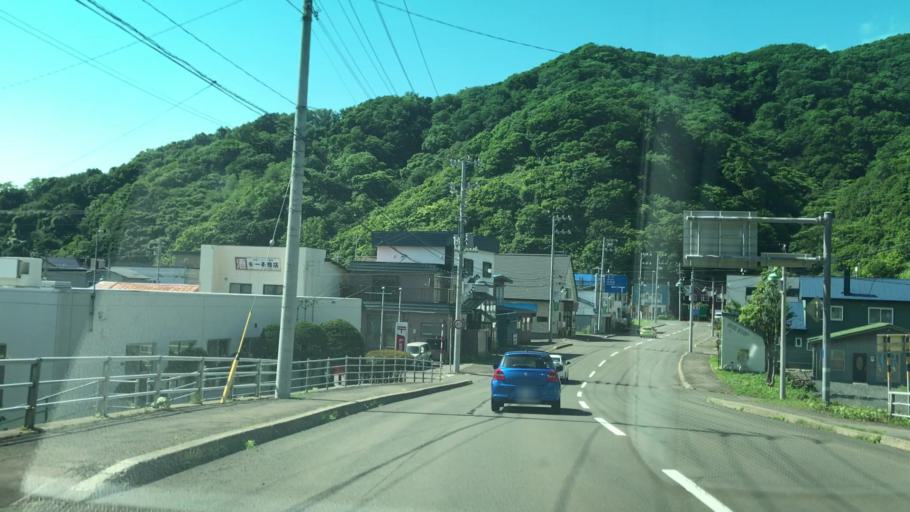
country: JP
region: Hokkaido
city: Iwanai
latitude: 43.1425
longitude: 140.4335
